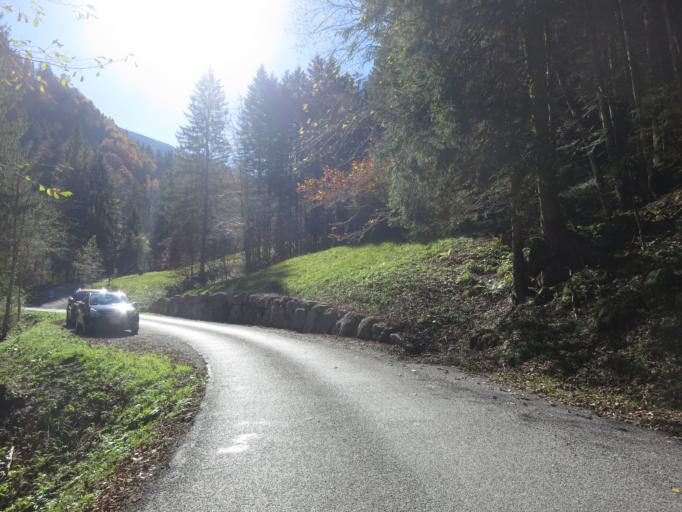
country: CH
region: Schwyz
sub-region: Bezirk March
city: Vorderthal
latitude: 47.0670
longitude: 8.9117
